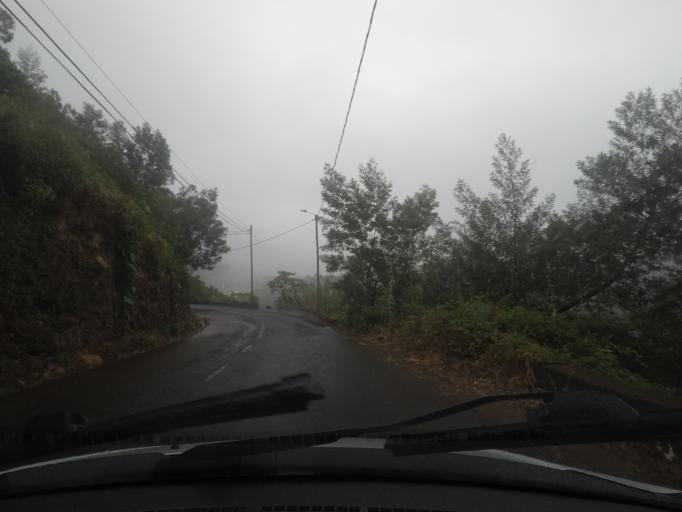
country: PT
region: Madeira
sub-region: Santana
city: Santana
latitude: 32.7828
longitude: -16.8596
